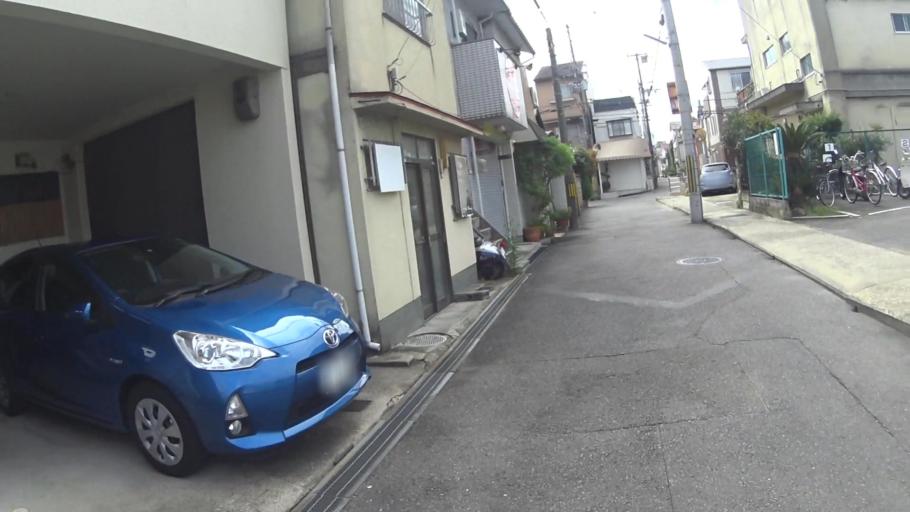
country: JP
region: Kyoto
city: Muko
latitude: 34.9519
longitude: 135.7059
